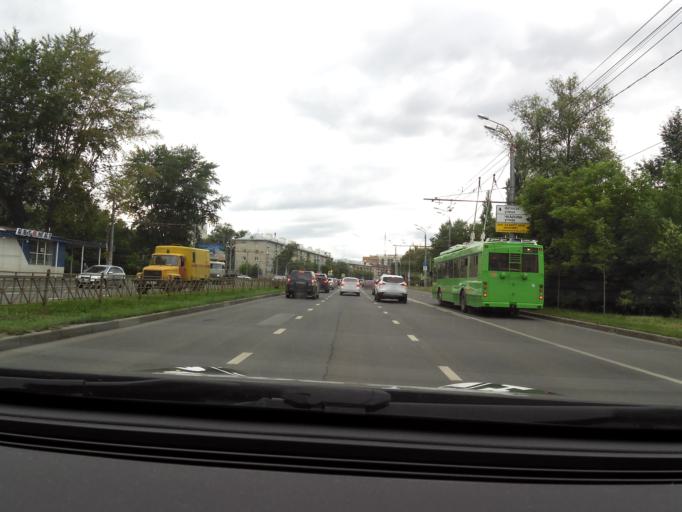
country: RU
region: Tatarstan
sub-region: Gorod Kazan'
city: Kazan
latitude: 55.8180
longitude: 49.0602
